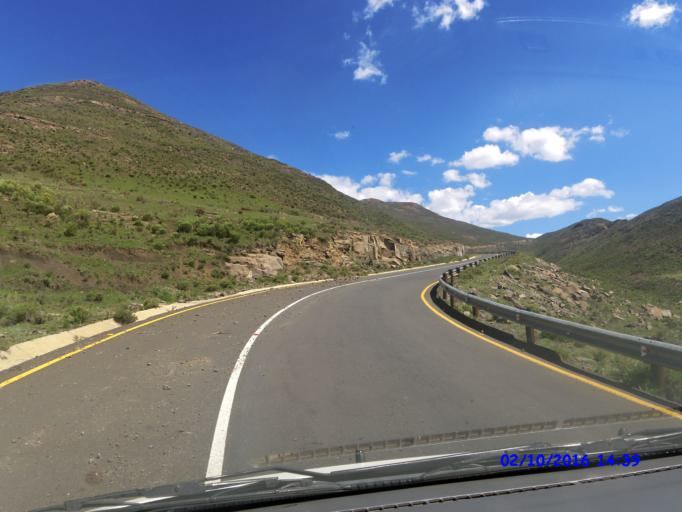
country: LS
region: Maseru
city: Nako
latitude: -29.5173
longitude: 28.0613
